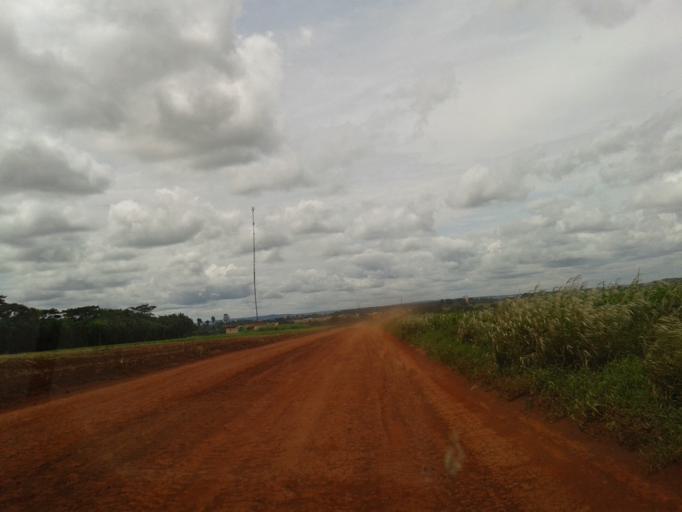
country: BR
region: Minas Gerais
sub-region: Centralina
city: Centralina
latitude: -18.5937
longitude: -49.2251
